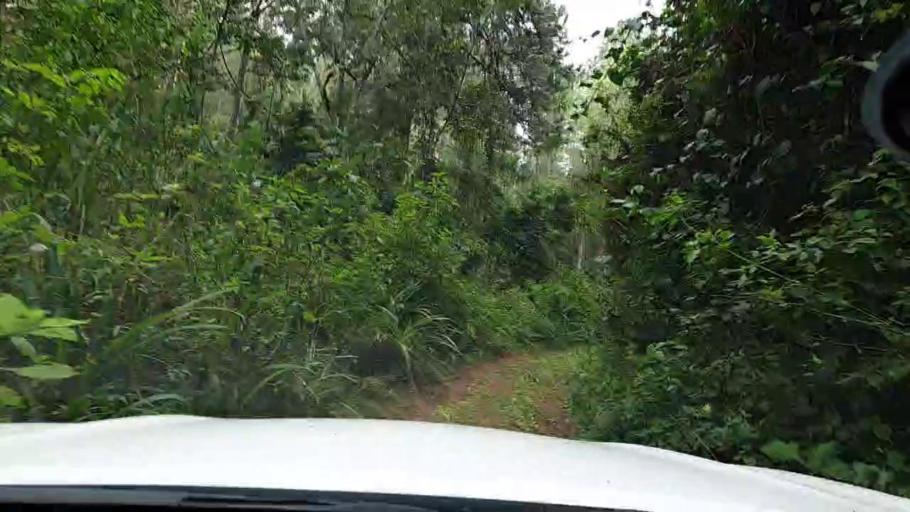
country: RW
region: Western Province
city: Kibuye
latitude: -2.2914
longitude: 29.3048
